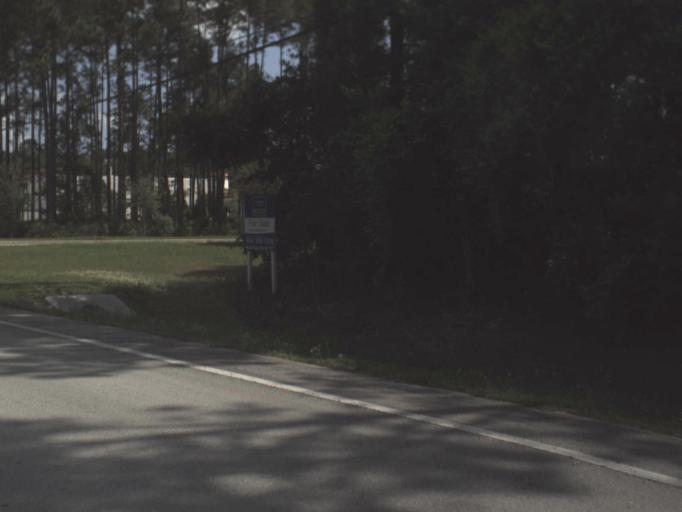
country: US
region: Florida
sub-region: Saint Johns County
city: Saint Augustine Shores
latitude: 29.7985
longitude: -81.3199
